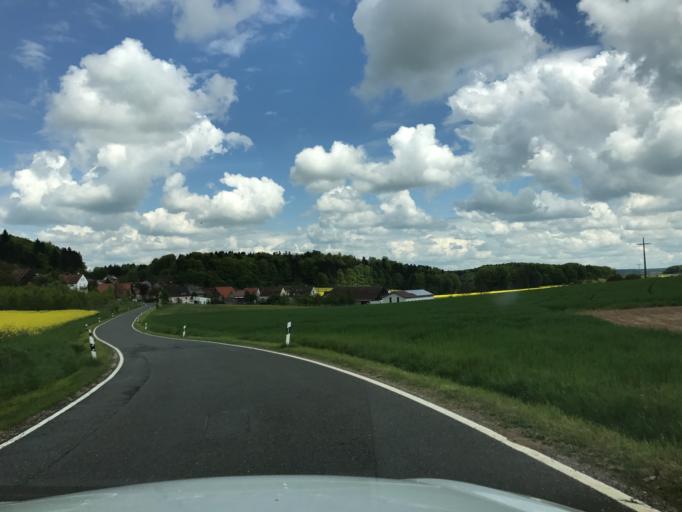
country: DE
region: Bavaria
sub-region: Upper Franconia
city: Leutenbach
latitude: 49.7082
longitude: 11.2126
